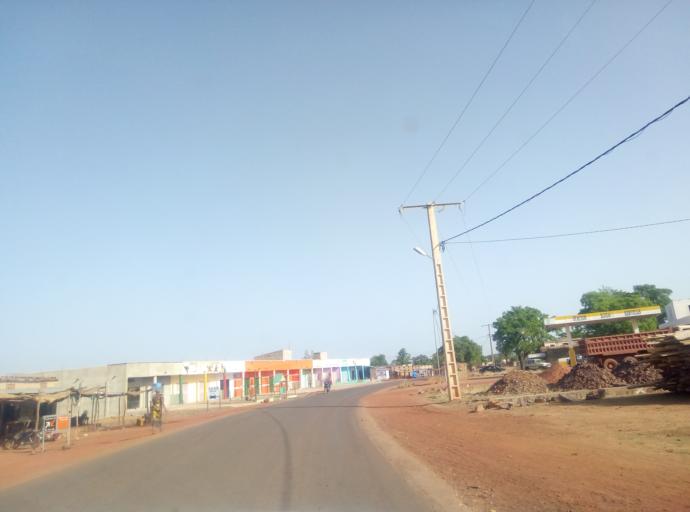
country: ML
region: Bamako
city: Bamako
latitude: 12.5969
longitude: -7.7669
